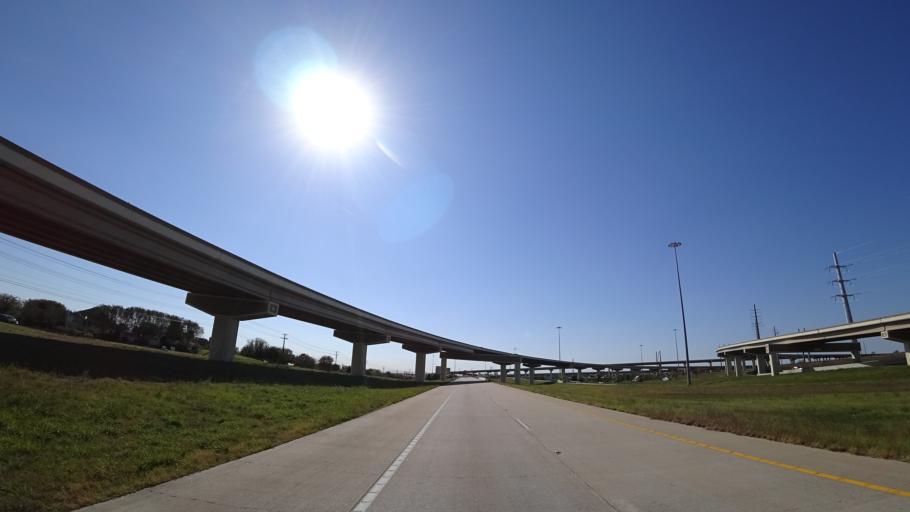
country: US
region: Texas
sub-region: Travis County
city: Pflugerville
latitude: 30.4763
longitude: -97.5897
